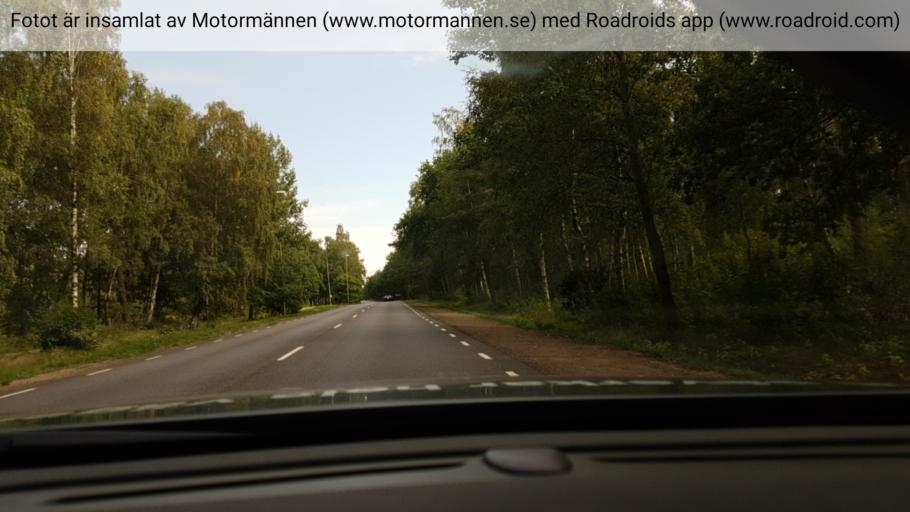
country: SE
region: Halland
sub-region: Halmstads Kommun
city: Mjallby
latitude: 56.6564
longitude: 12.7607
